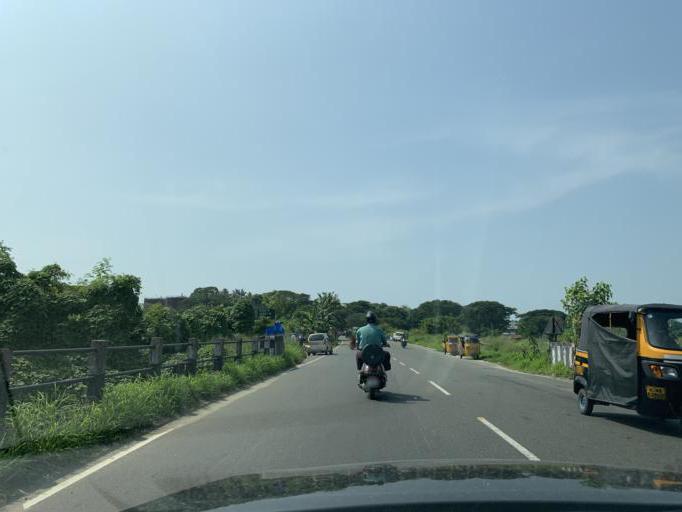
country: IN
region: Kerala
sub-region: Ernakulam
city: Cochin
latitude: 9.9368
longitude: 76.2745
